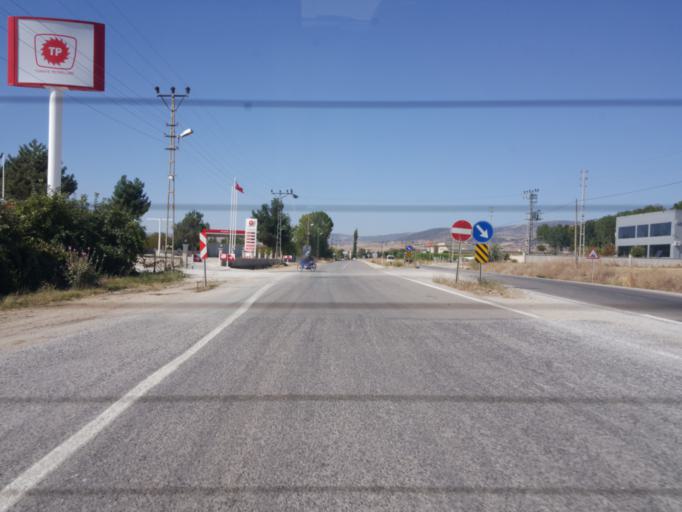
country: TR
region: Tokat
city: Zile
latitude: 40.3102
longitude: 35.9128
